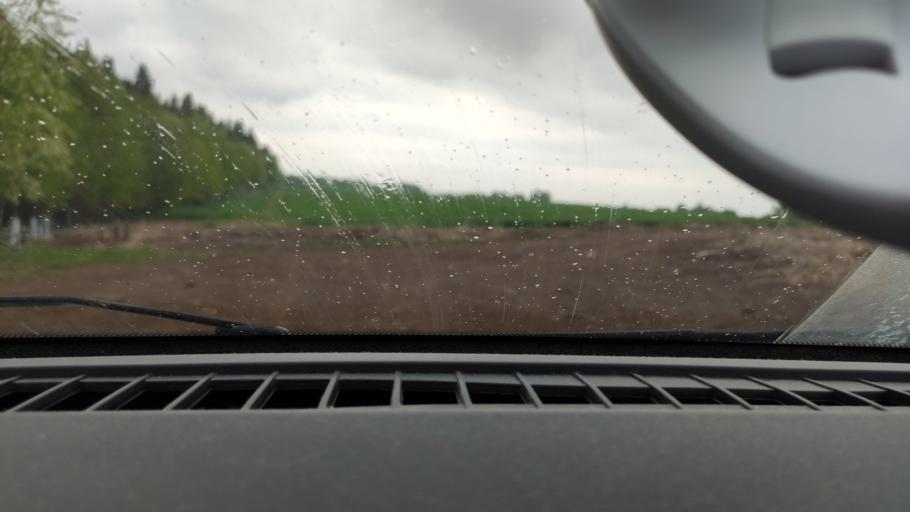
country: RU
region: Perm
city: Gamovo
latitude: 57.8512
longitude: 56.0741
